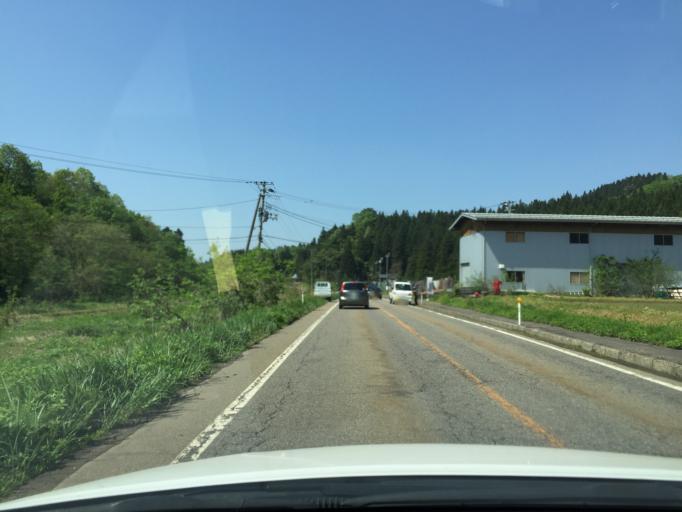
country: JP
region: Niigata
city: Muramatsu
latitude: 37.6425
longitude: 139.1151
